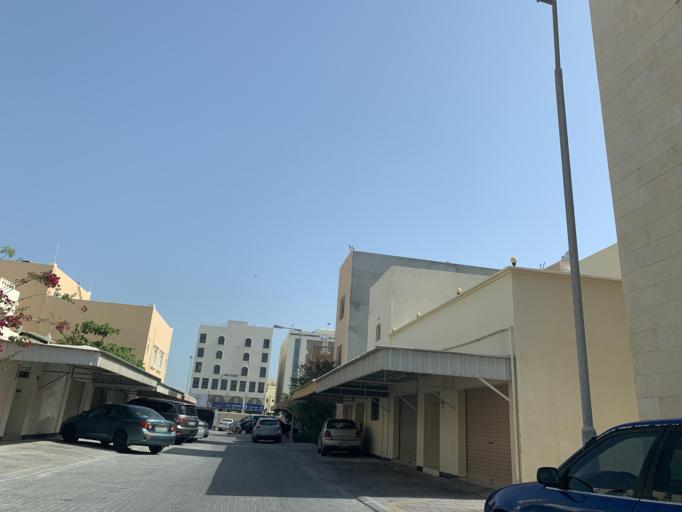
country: BH
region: Muharraq
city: Al Muharraq
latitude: 26.2718
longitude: 50.5992
